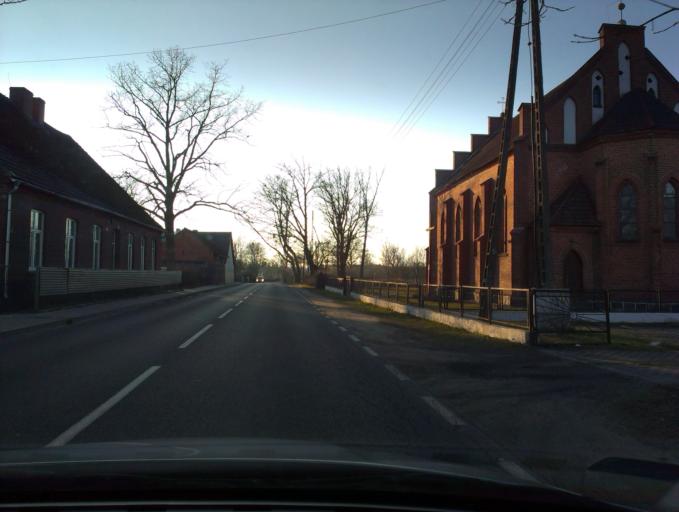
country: PL
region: West Pomeranian Voivodeship
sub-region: Powiat szczecinecki
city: Szczecinek
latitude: 53.6518
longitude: 16.6285
